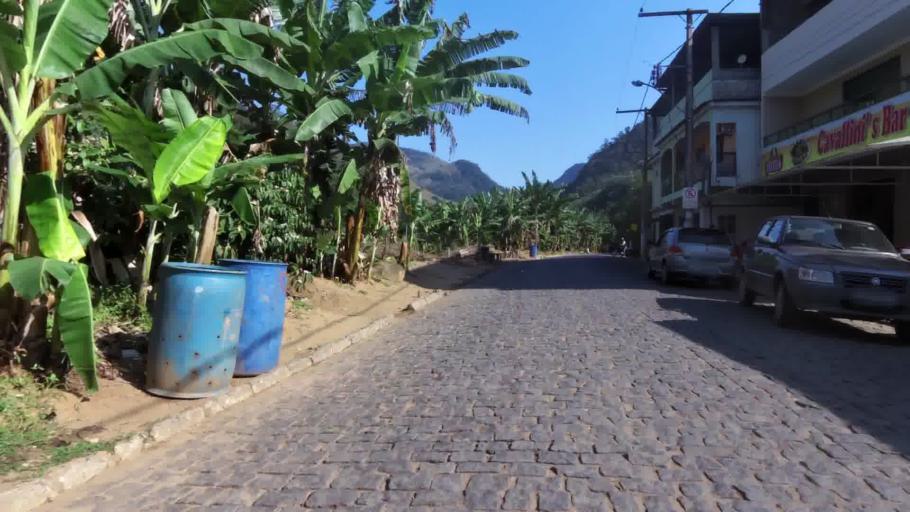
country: BR
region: Espirito Santo
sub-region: Alfredo Chaves
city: Alfredo Chaves
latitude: -20.6284
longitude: -40.7657
